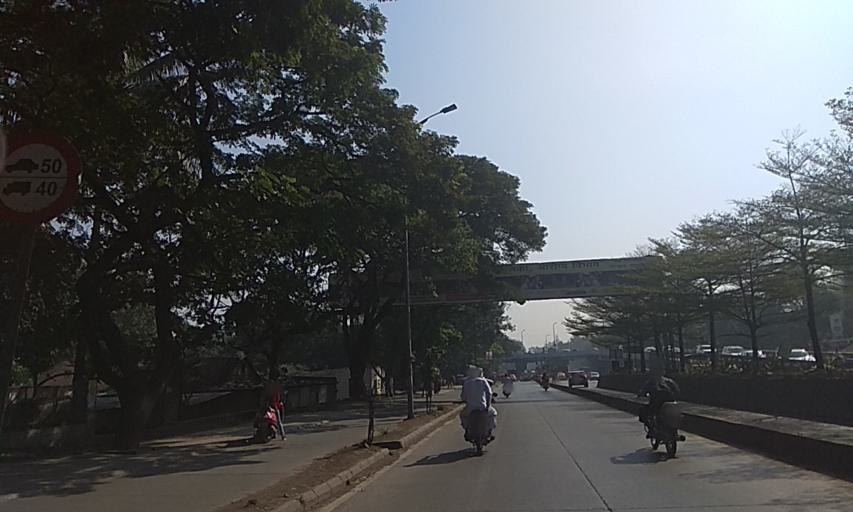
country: IN
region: Maharashtra
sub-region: Pune Division
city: Pune
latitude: 18.5030
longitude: 73.9255
